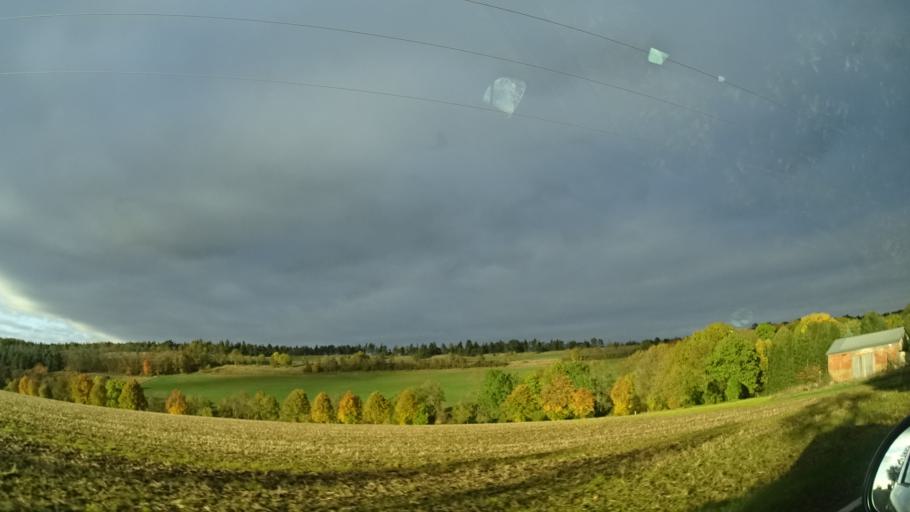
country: DE
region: Thuringia
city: Blankenhain
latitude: 50.8418
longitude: 11.3675
